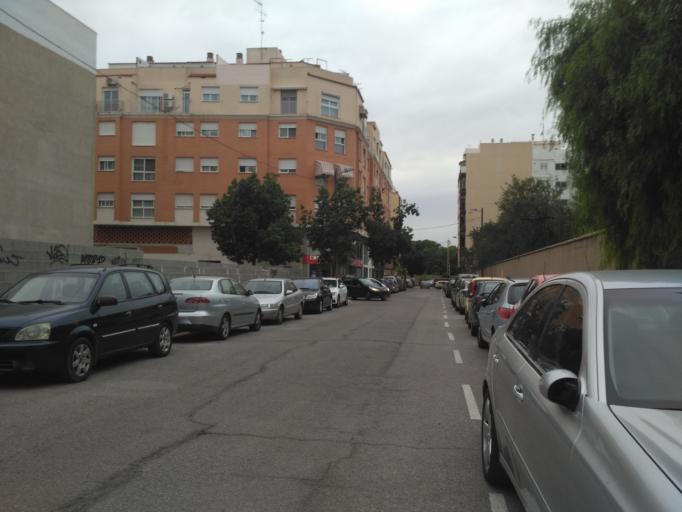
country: ES
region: Valencia
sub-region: Provincia de Castello
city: Castello de la Plana
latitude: 39.9854
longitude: -0.0520
